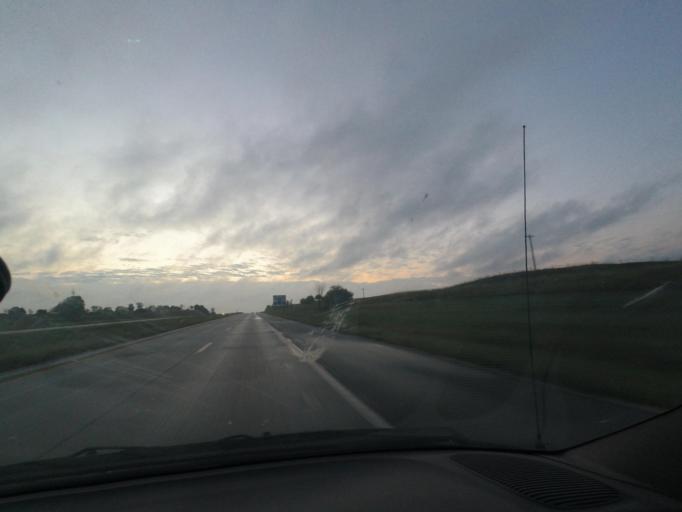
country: US
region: Missouri
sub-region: Linn County
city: Marceline
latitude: 39.7611
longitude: -92.9570
